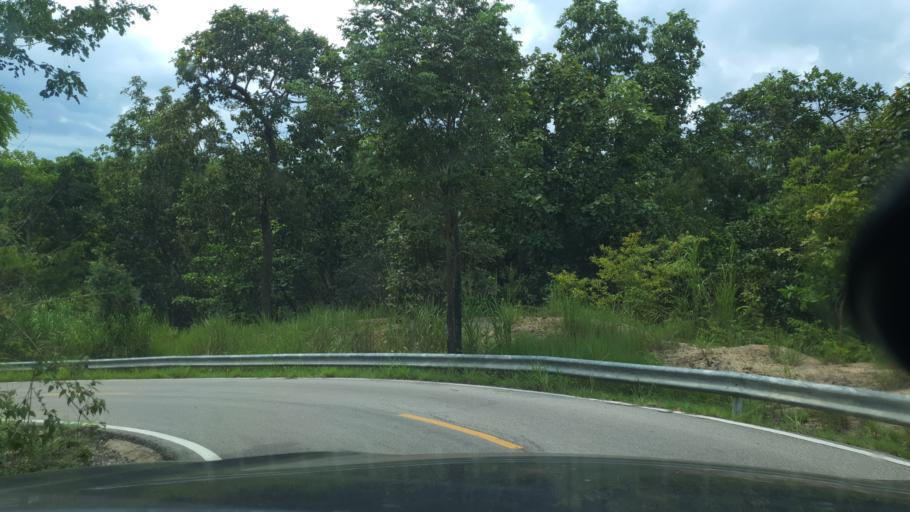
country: TH
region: Lamphun
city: Mae Tha
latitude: 18.5149
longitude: 99.2625
